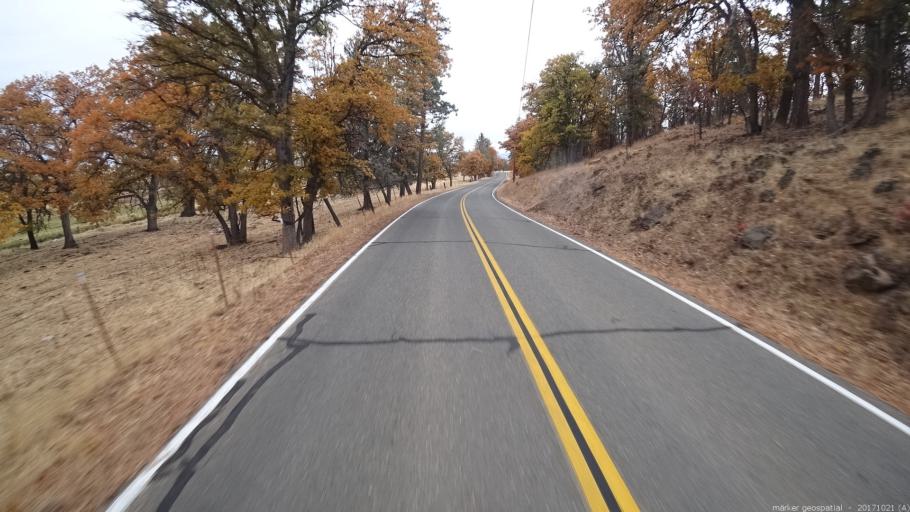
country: US
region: California
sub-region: Shasta County
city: Burney
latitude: 41.0045
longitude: -121.4306
